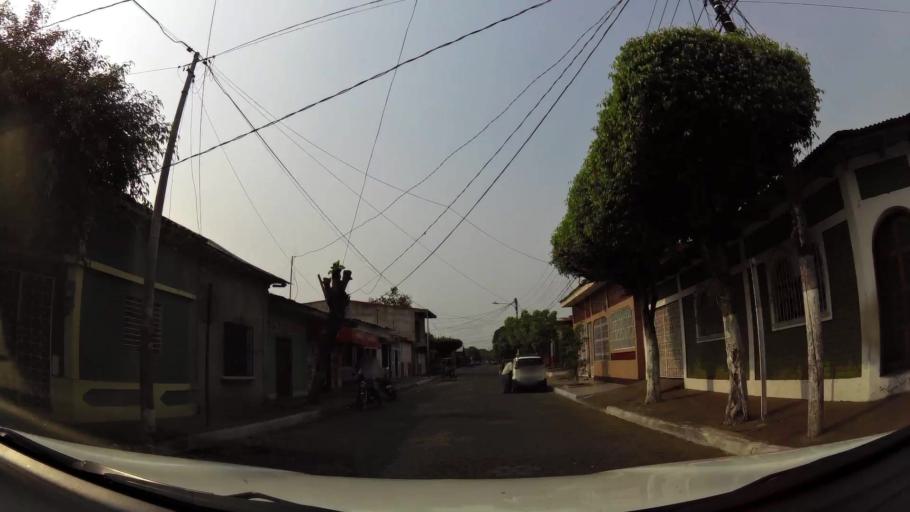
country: NI
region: Chinandega
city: Chinandega
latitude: 12.6322
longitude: -87.1230
